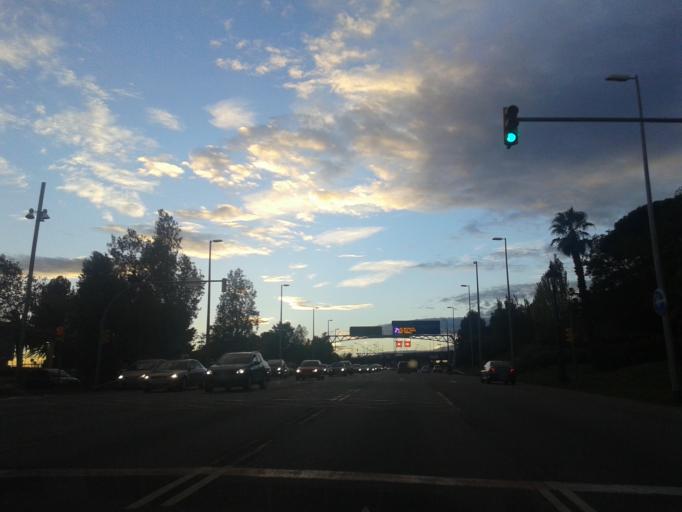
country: ES
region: Catalonia
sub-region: Provincia de Barcelona
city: Esplugues de Llobregat
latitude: 41.3832
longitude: 2.1071
